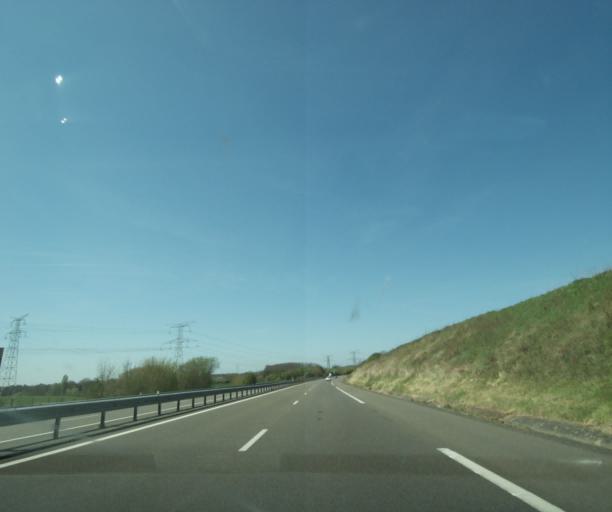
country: FR
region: Bourgogne
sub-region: Departement de la Nievre
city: Coulanges-les-Nevers
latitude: 47.0252
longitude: 3.1762
